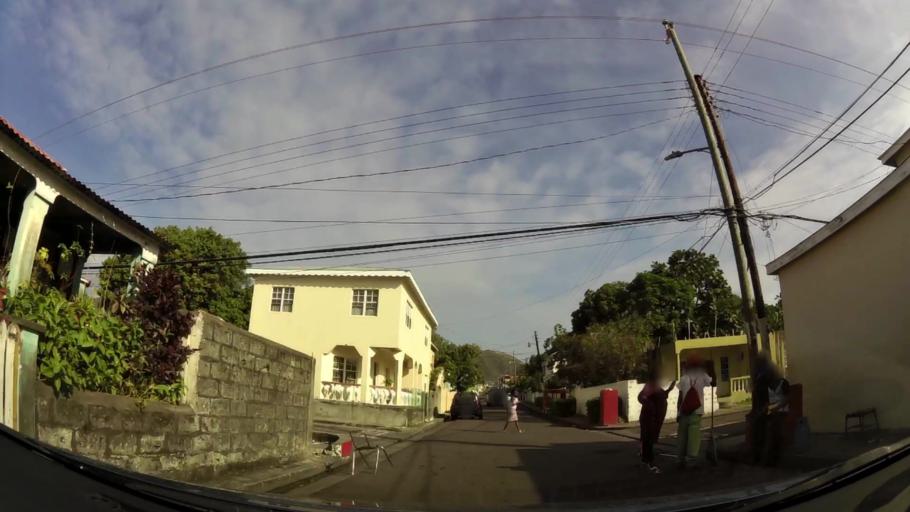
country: KN
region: Saint George Basseterre
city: Basseterre
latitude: 17.2925
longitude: -62.7353
